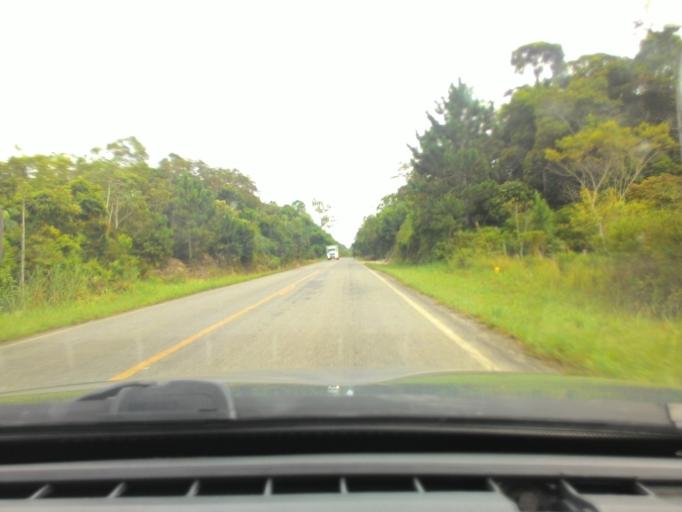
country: BR
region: Sao Paulo
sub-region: Pariquera-Acu
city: Pariquera Acu
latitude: -24.7670
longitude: -47.7829
